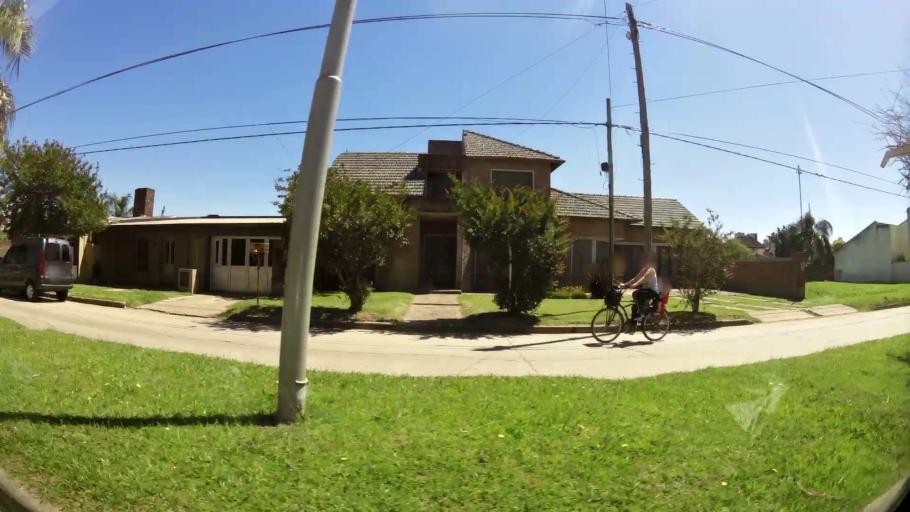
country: AR
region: Santa Fe
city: Esperanza
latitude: -31.4526
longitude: -60.9146
